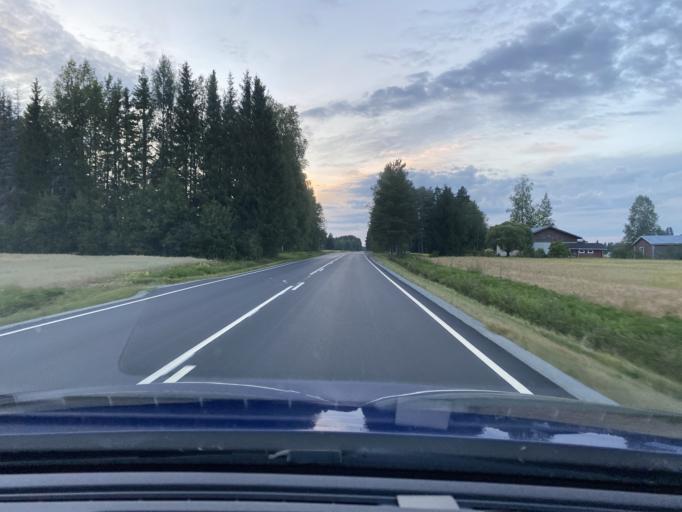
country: FI
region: Satakunta
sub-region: Pohjois-Satakunta
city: Honkajoki
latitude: 62.0892
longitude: 22.2470
